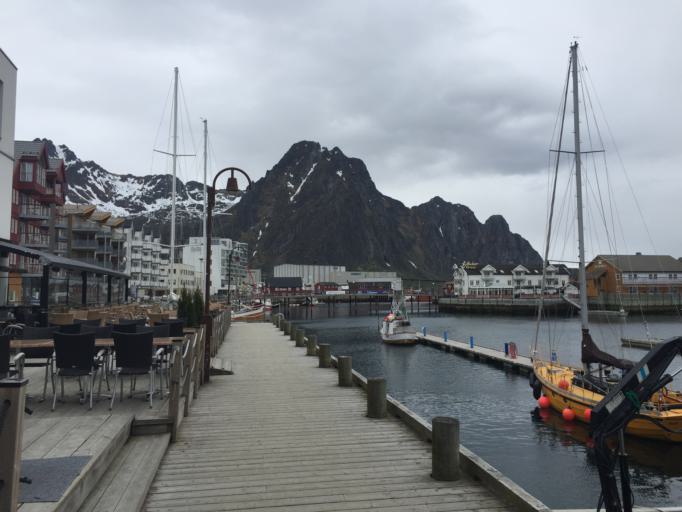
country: NO
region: Nordland
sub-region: Vagan
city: Svolvaer
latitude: 68.2324
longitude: 14.5664
